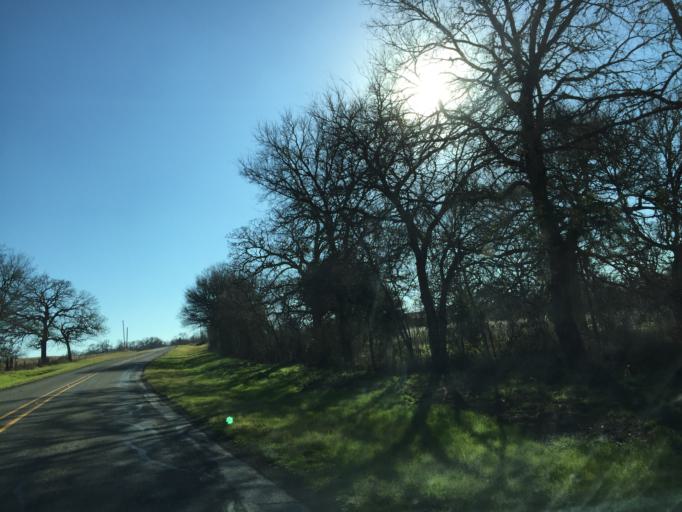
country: US
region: Texas
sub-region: Bastrop County
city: Elgin
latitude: 30.4307
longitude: -97.2590
